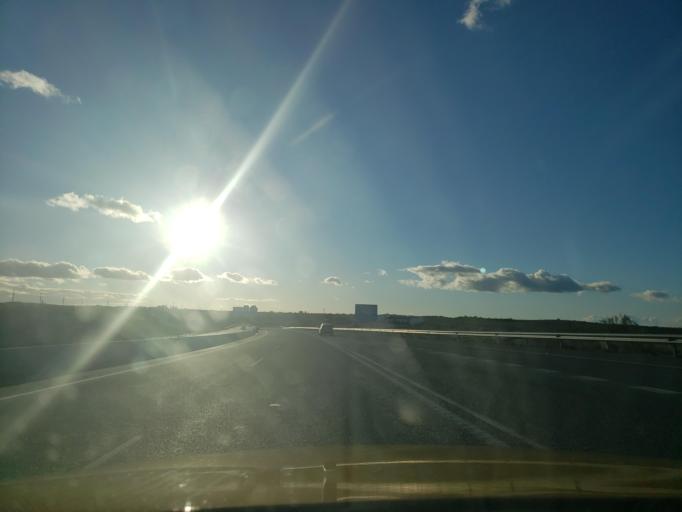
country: ES
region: Castille-La Mancha
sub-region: Province of Toledo
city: Burguillos de Toledo
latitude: 39.8146
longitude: -3.9932
